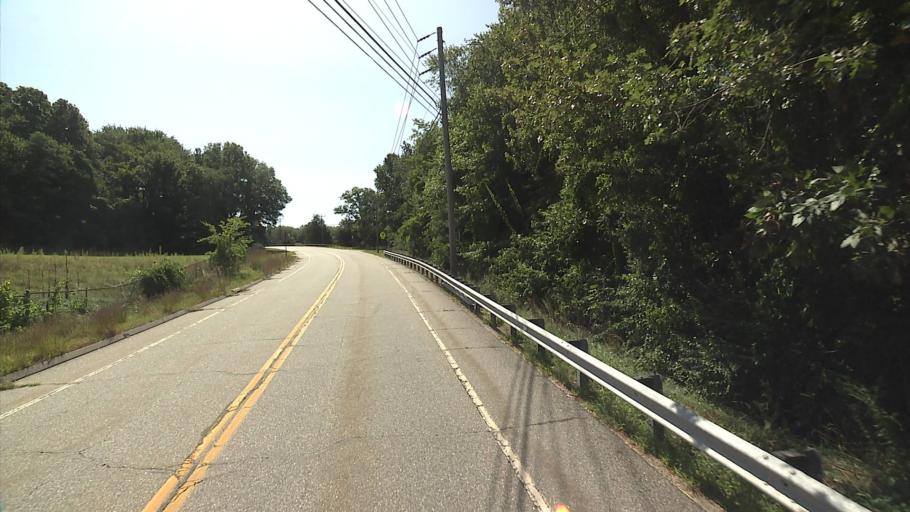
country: US
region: Connecticut
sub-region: New London County
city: Baltic
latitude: 41.6307
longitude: -72.1274
